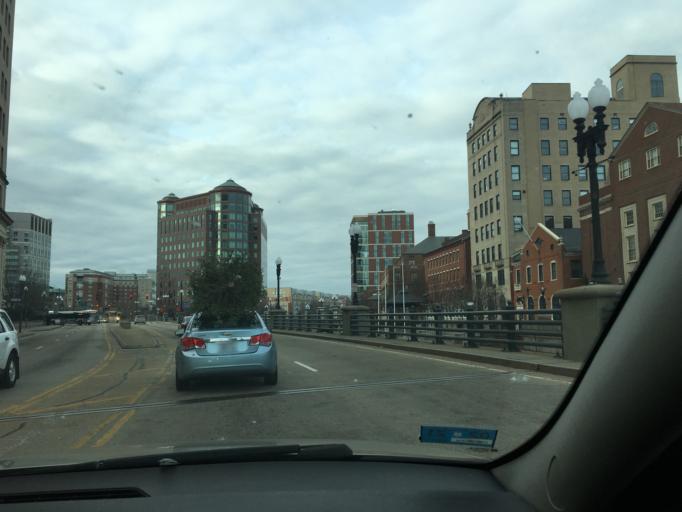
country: US
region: Rhode Island
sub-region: Providence County
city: Providence
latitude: 41.8255
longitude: -71.4089
